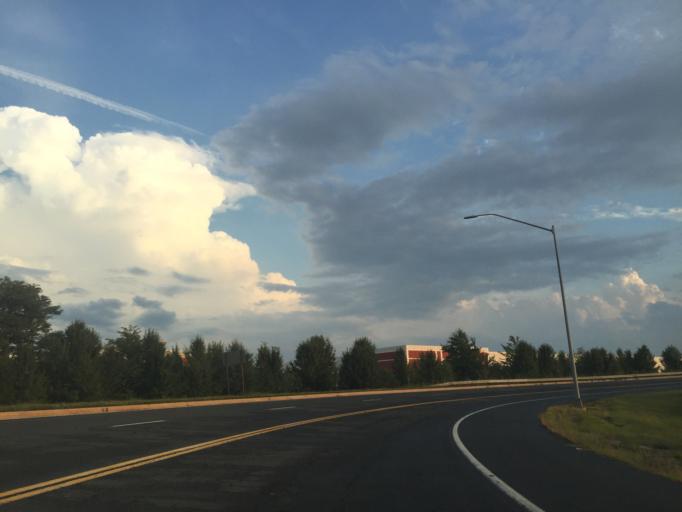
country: US
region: Maryland
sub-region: Harford County
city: Riverside
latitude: 39.4707
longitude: -76.2319
